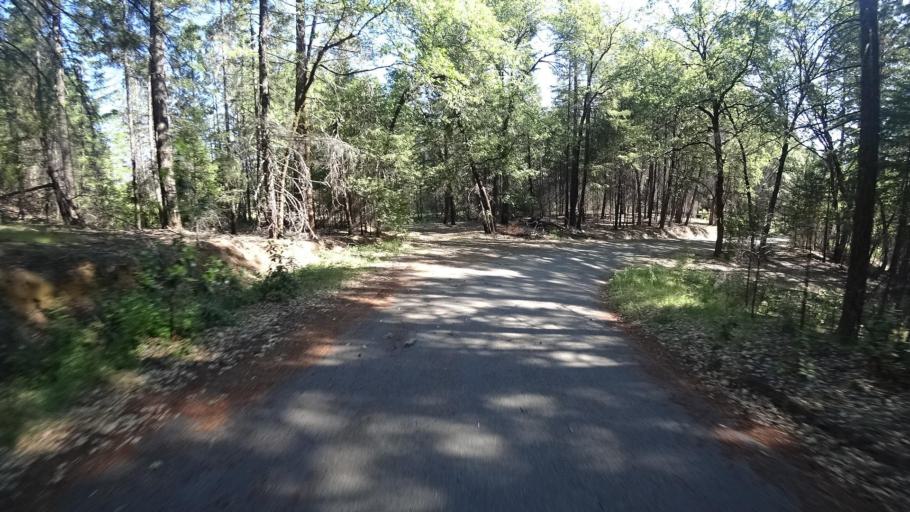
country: US
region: California
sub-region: Lake County
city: Upper Lake
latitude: 39.3992
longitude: -122.9599
